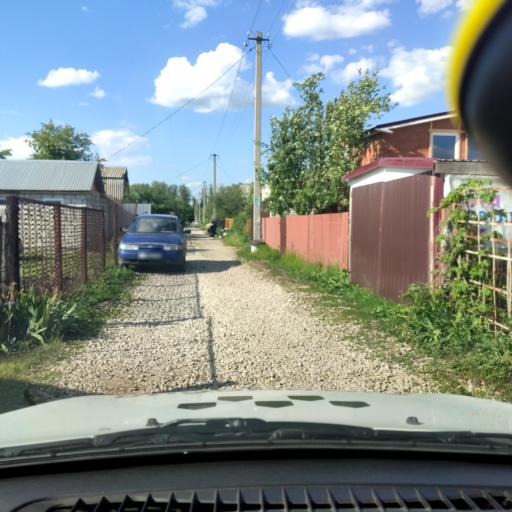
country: RU
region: Samara
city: Tol'yatti
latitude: 53.5975
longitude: 49.2939
